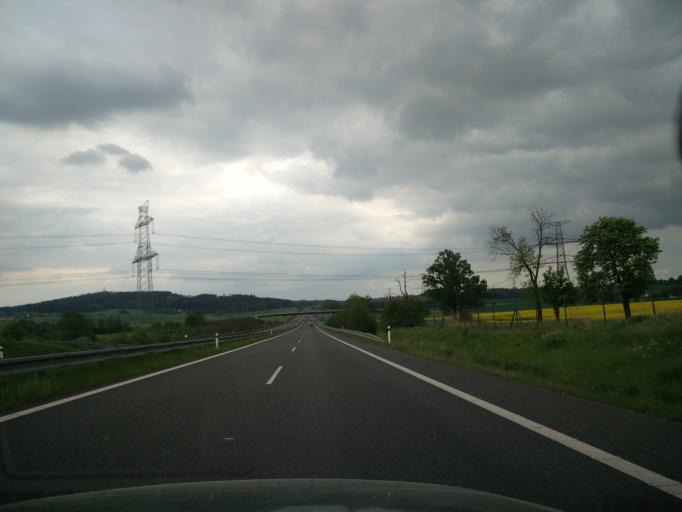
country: CZ
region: Jihocesky
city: Mirotice
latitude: 49.3797
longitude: 14.0509
